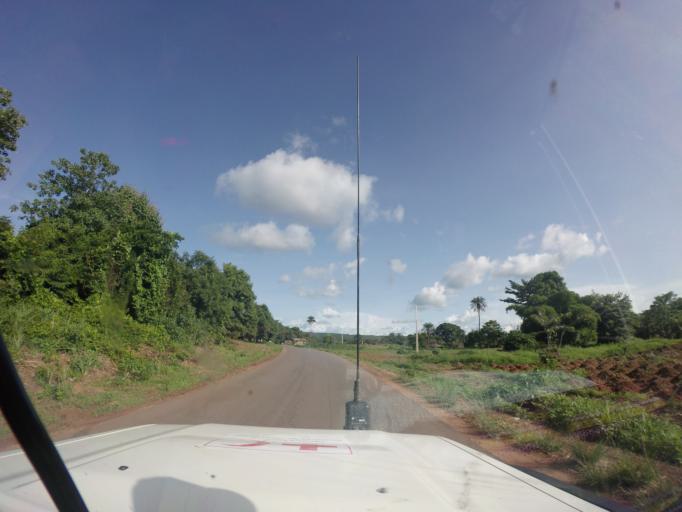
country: GN
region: Kindia
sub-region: Kindia
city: Kindia
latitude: 10.1077
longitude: -12.5656
